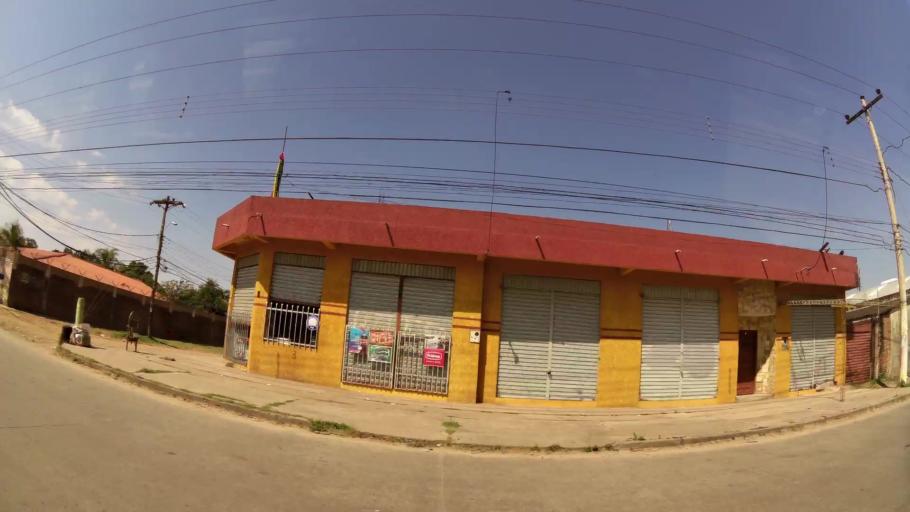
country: BO
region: Santa Cruz
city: Santa Cruz de la Sierra
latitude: -17.7360
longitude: -63.1533
